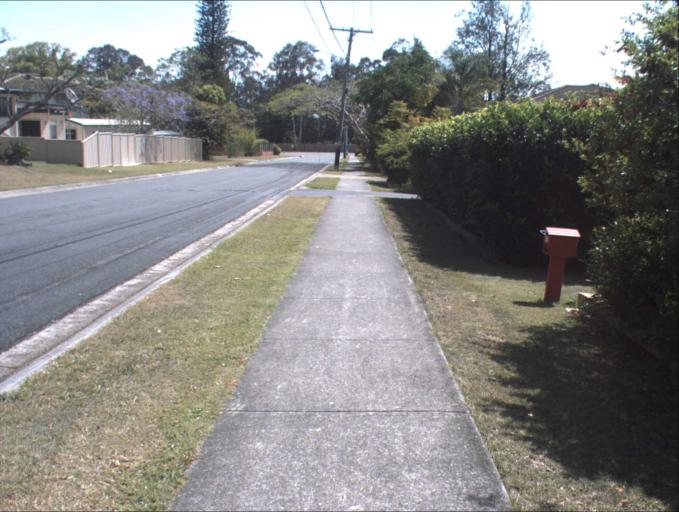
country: AU
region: Queensland
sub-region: Logan
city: Slacks Creek
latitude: -27.6375
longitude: 153.1518
